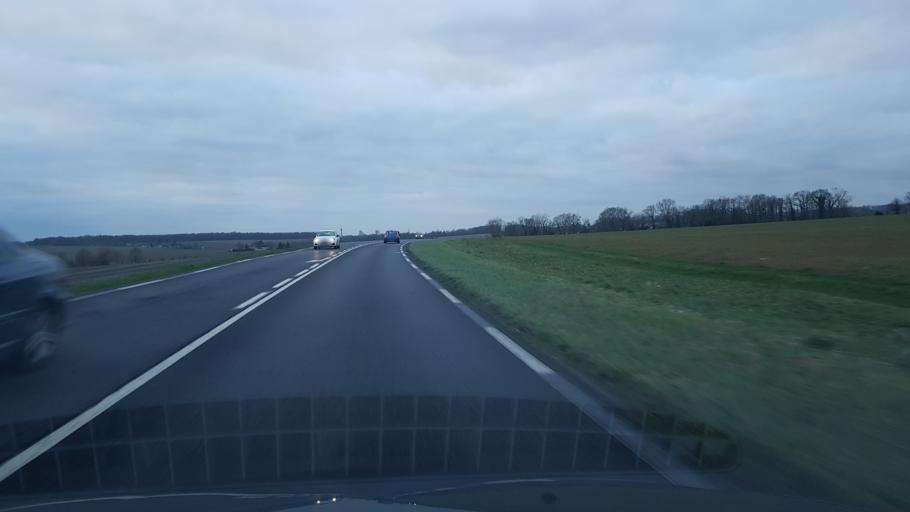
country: FR
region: Ile-de-France
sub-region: Departement de Seine-et-Marne
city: La Ferte-Gaucher
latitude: 48.6973
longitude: 3.2837
